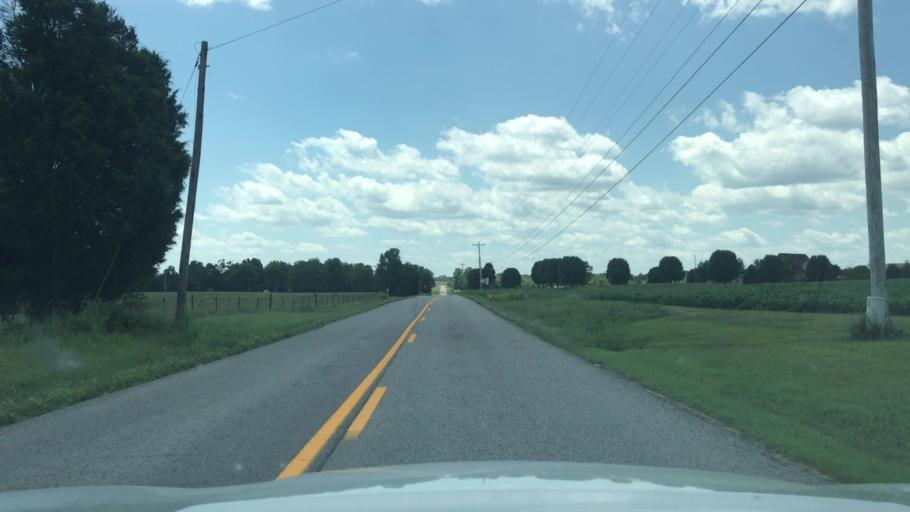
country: US
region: Kentucky
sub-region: Christian County
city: Hopkinsville
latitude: 36.9680
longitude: -87.3814
